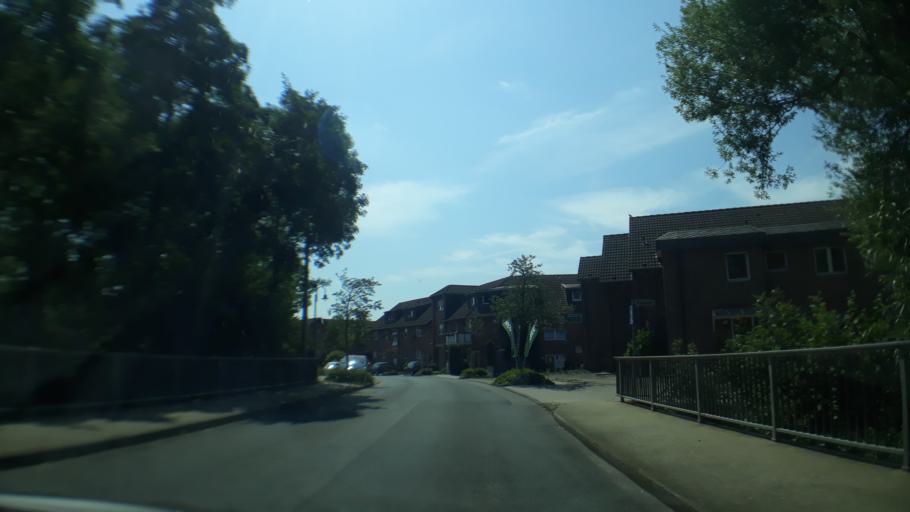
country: DE
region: North Rhine-Westphalia
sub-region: Regierungsbezirk Koln
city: Inden
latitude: 50.8438
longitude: 6.3575
